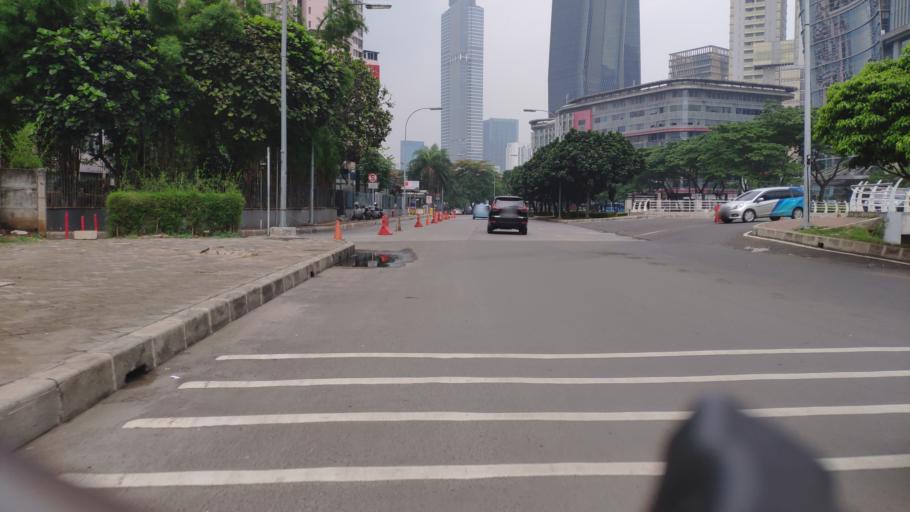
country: ID
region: Jakarta Raya
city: Jakarta
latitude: -6.2159
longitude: 106.8364
